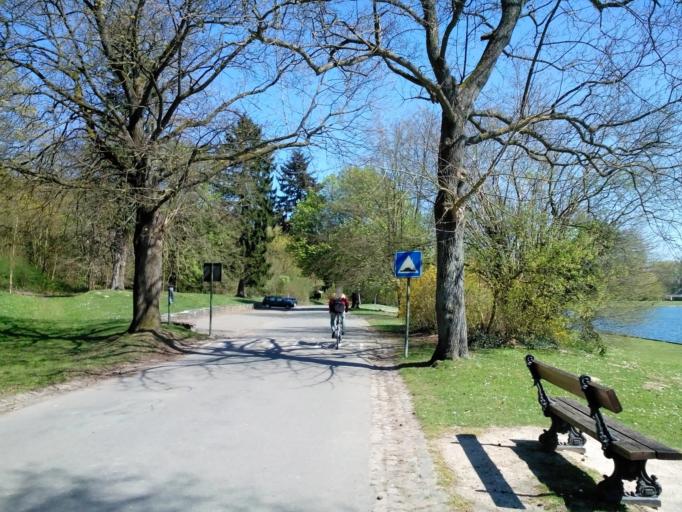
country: BE
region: Flanders
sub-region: Provincie Vlaams-Brabant
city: Tervuren
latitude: 50.8320
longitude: 4.5421
